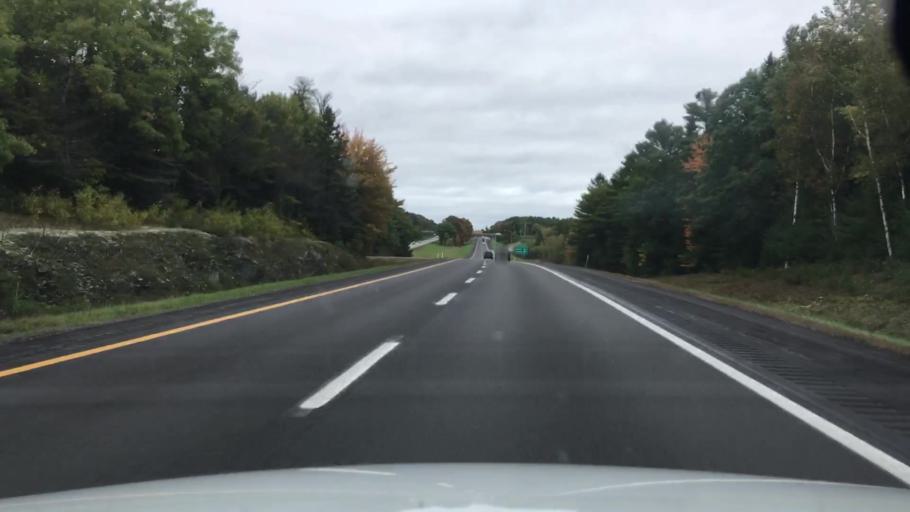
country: US
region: Maine
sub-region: Penobscot County
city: Veazie
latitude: 44.8667
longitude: -68.7074
